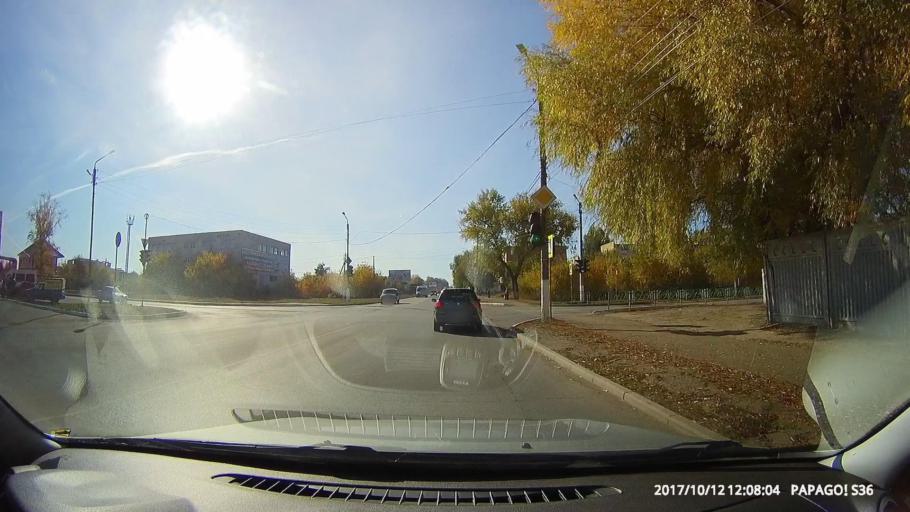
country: RU
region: Samara
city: Chapayevsk
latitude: 52.9644
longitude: 49.6985
